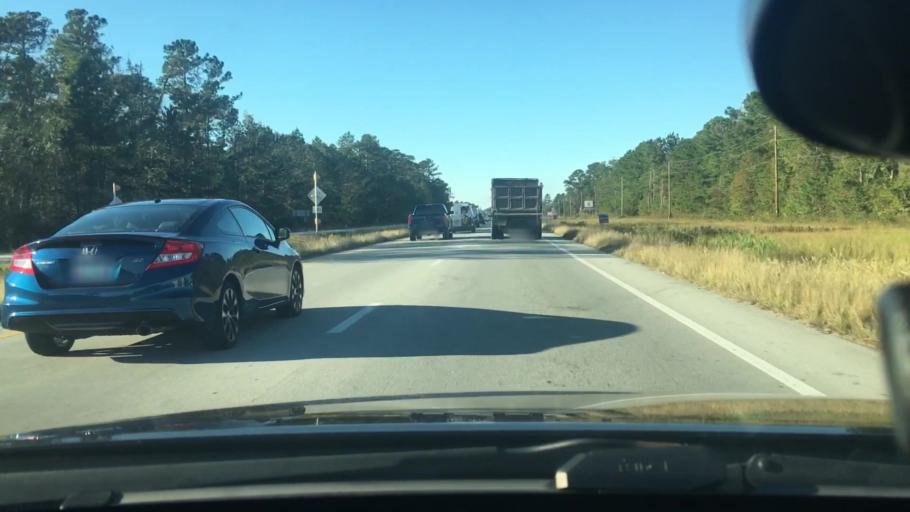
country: US
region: North Carolina
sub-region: Craven County
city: James City
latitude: 35.0514
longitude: -77.0148
